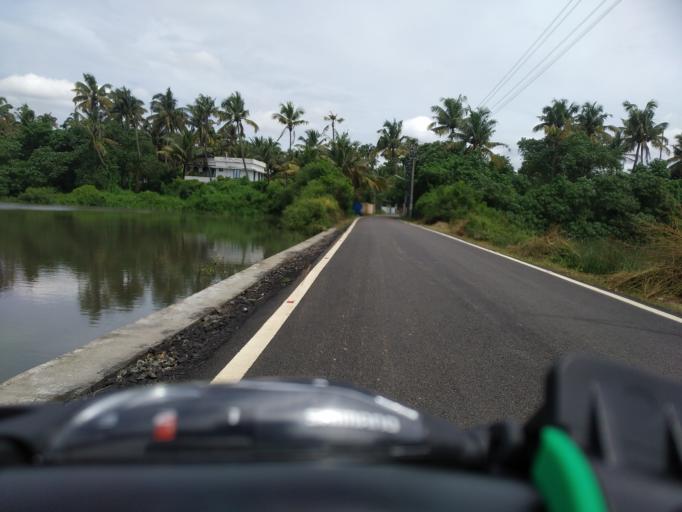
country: IN
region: Kerala
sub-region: Ernakulam
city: Elur
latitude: 10.0810
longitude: 76.2186
